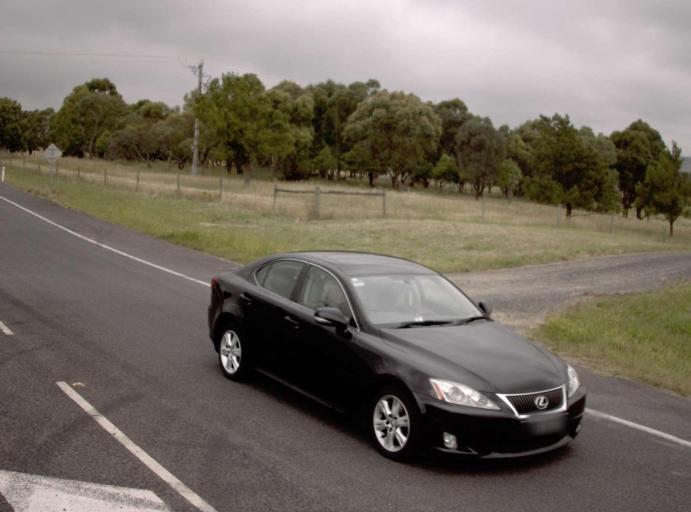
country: AU
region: Victoria
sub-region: Latrobe
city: Traralgon
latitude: -38.2471
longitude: 146.5475
